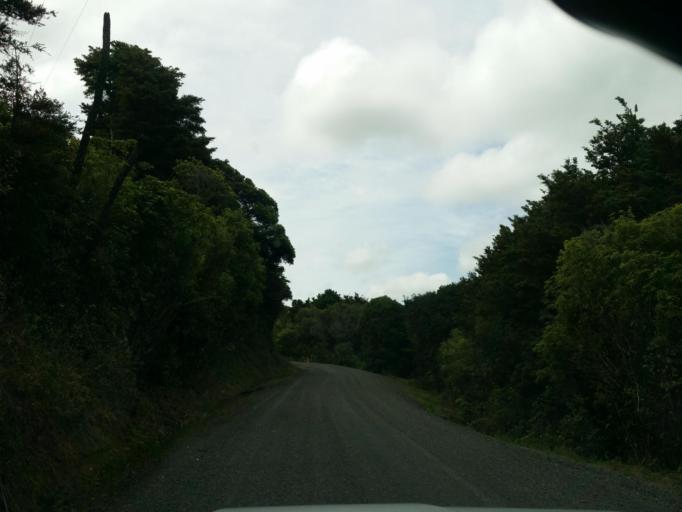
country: NZ
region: Northland
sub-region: Whangarei
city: Maungatapere
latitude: -35.9011
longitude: 174.1070
